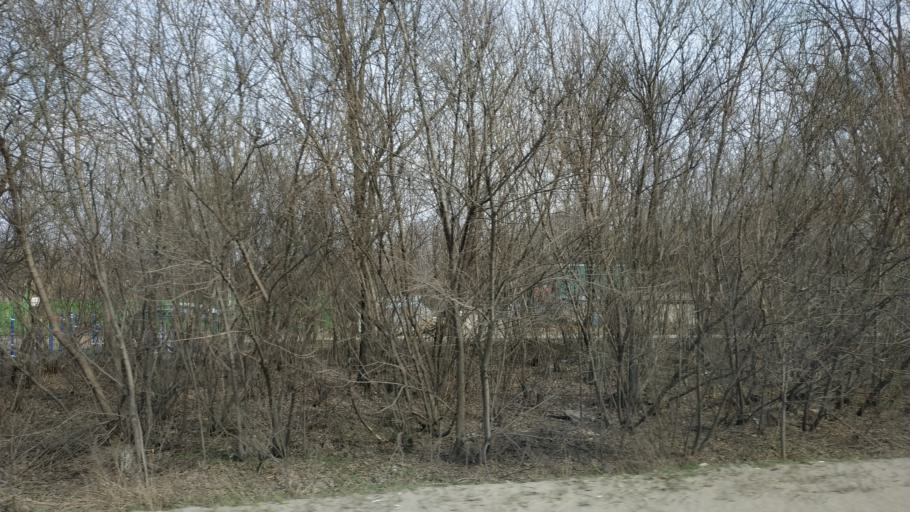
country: RU
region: Moskovskaya
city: Bronnitsy
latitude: 55.4038
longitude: 38.3030
